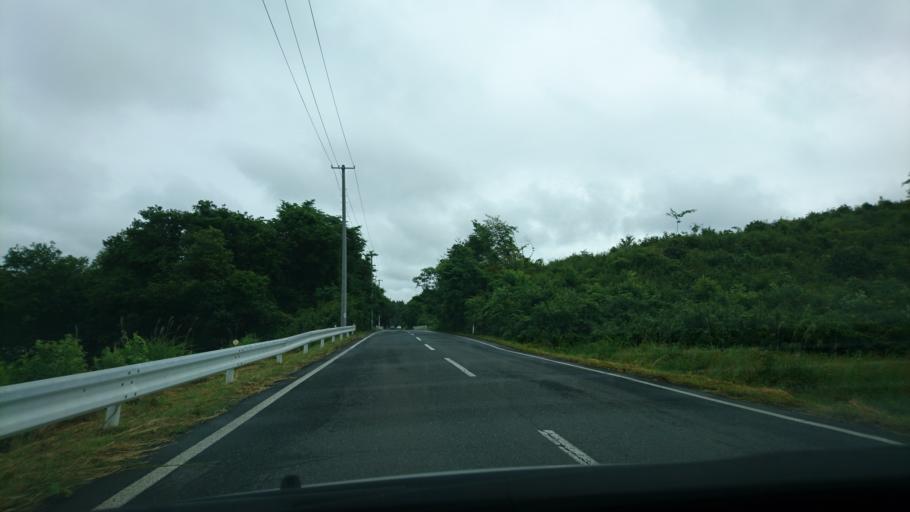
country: JP
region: Iwate
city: Ichinoseki
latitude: 38.8880
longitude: 141.1483
